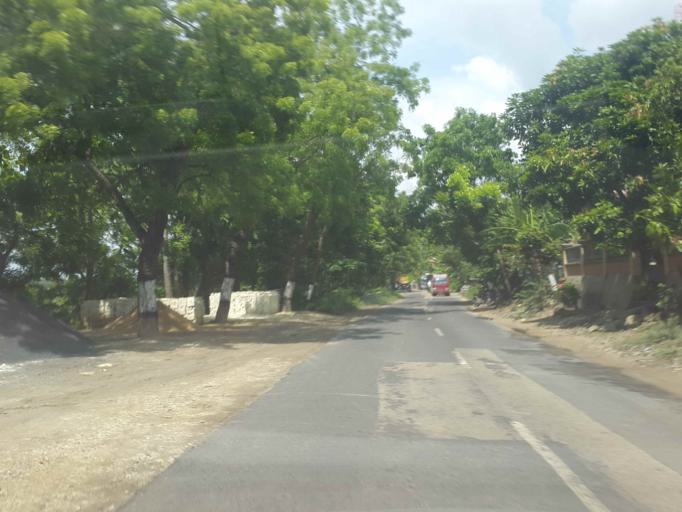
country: ID
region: East Java
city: Batojaran
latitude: -7.1088
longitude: 113.6851
